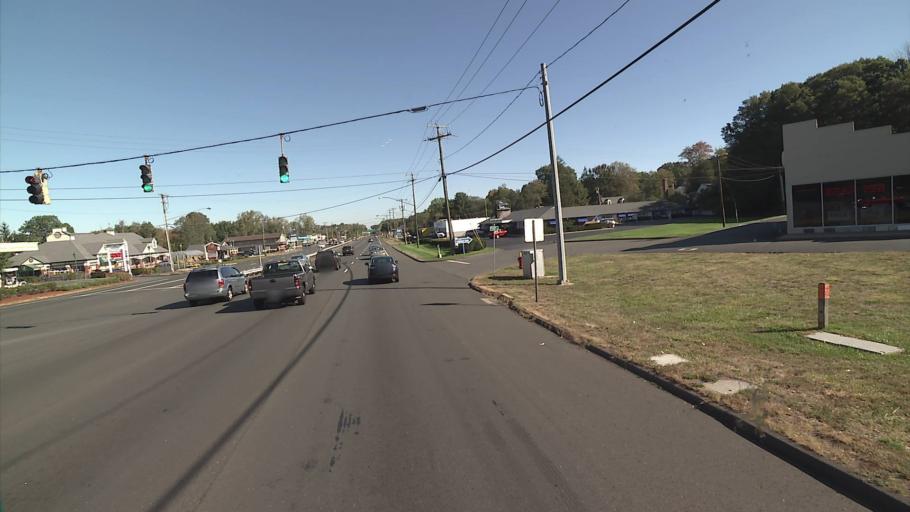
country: US
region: Connecticut
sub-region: Hartford County
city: Newington
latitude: 41.7032
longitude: -72.7028
